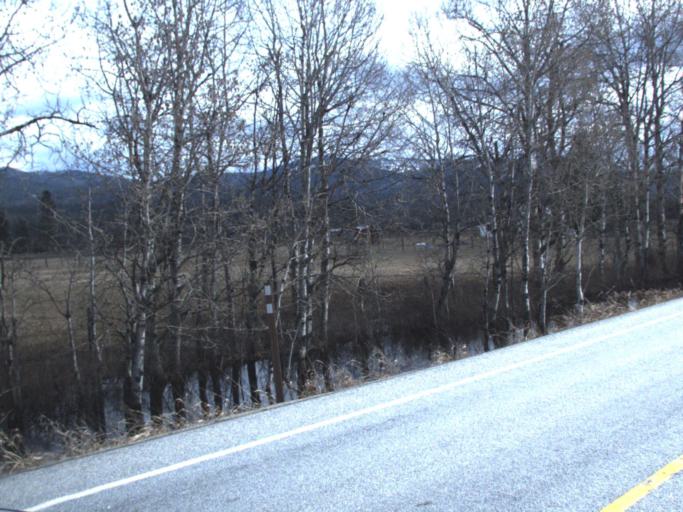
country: US
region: Washington
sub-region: Pend Oreille County
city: Newport
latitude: 48.2298
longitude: -117.1571
